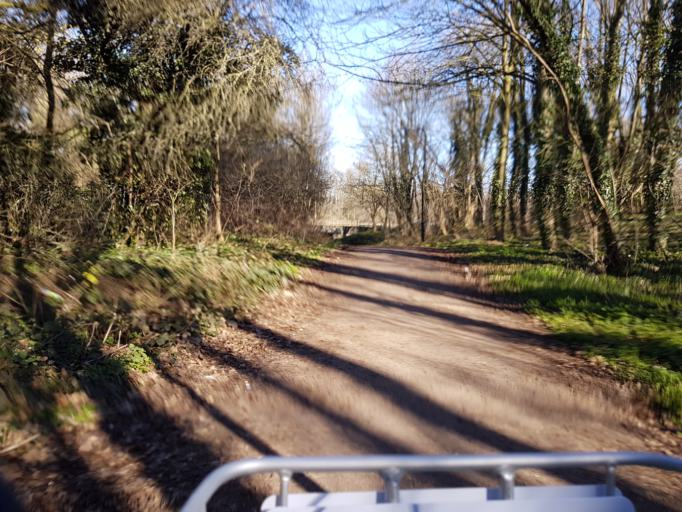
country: GB
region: England
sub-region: Milton Keynes
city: Milton Keynes
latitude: 52.0201
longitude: -0.7525
